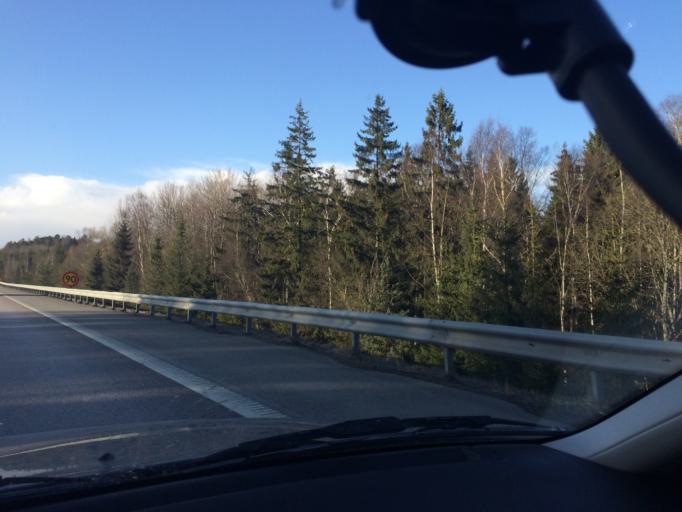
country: SE
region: Stockholm
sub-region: Jarfalla Kommun
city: Jakobsberg
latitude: 59.4298
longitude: 17.8486
